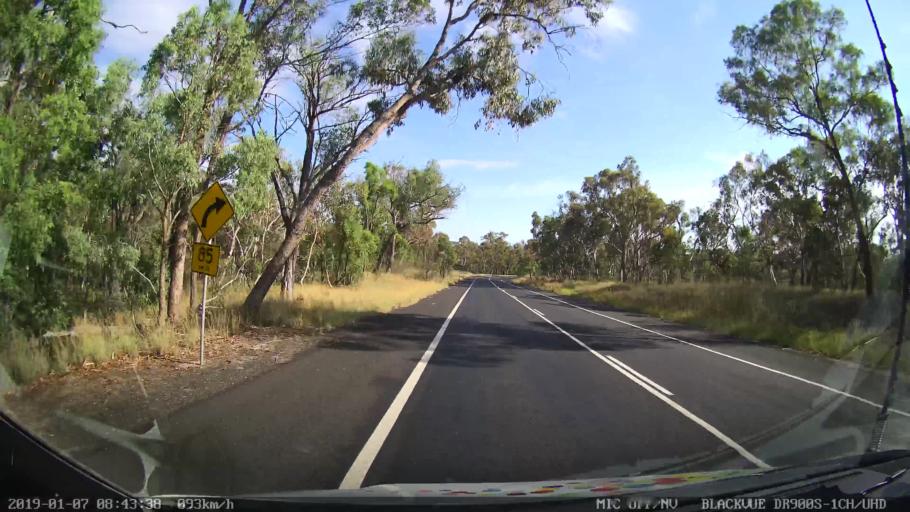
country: AU
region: New South Wales
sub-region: Tamworth Municipality
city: Kootingal
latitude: -30.8422
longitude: 151.2155
